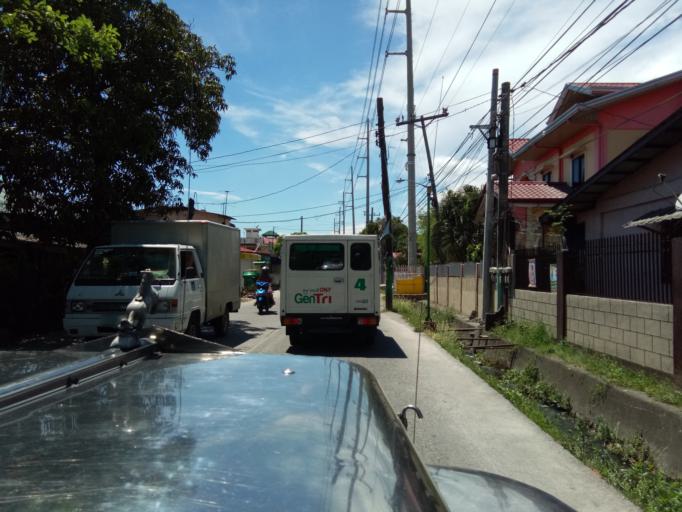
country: PH
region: Calabarzon
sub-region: Province of Cavite
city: General Trias
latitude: 14.3663
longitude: 120.8931
